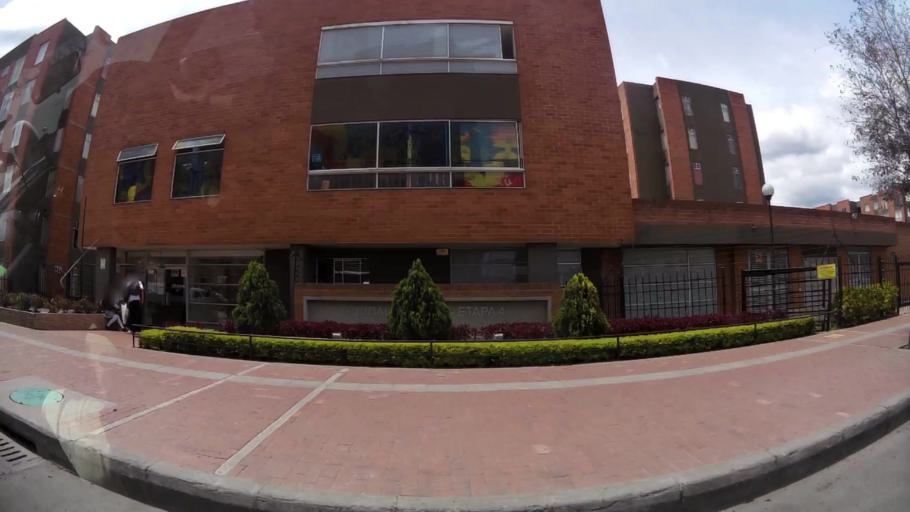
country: CO
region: Cundinamarca
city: Funza
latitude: 4.6505
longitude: -74.1635
